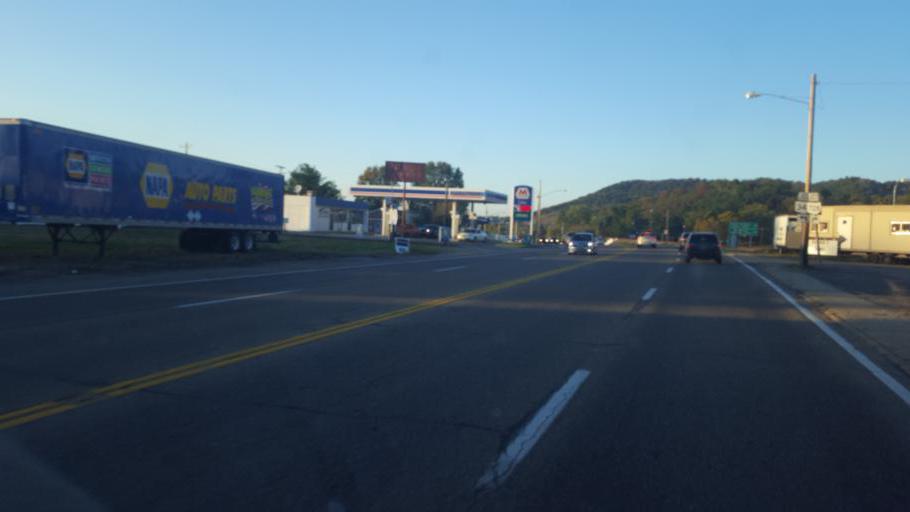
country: US
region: Ohio
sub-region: Scioto County
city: Lucasville
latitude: 38.8829
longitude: -82.9965
